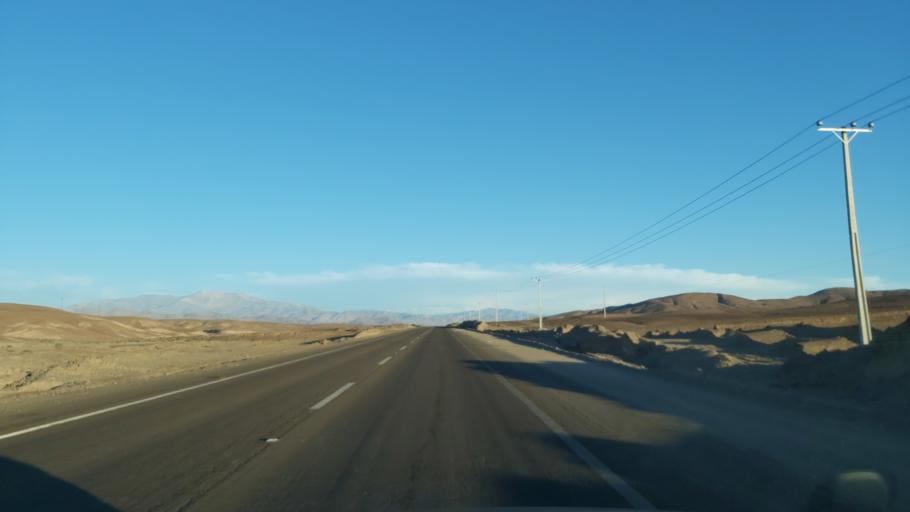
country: CL
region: Atacama
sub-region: Provincia de Chanaral
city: Diego de Almagro
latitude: -26.4291
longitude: -70.0134
